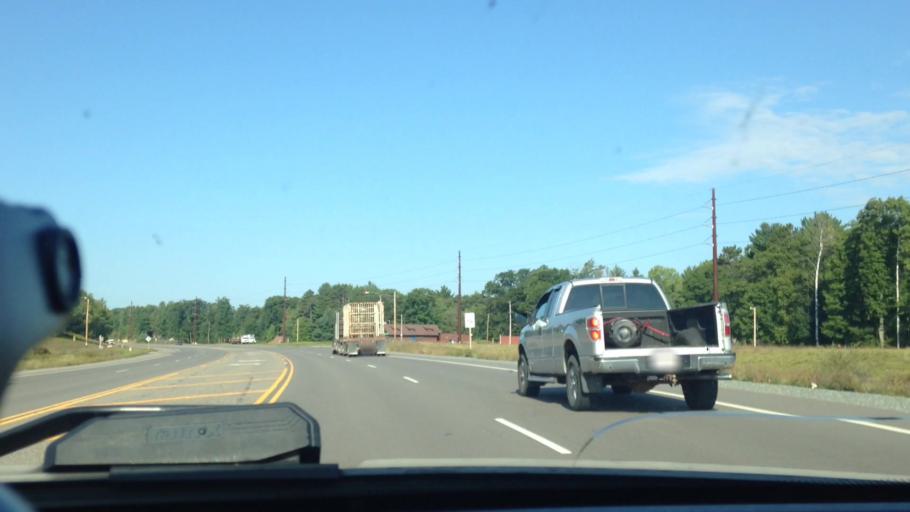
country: US
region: Michigan
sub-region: Dickinson County
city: Iron Mountain
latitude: 45.8816
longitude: -88.1277
